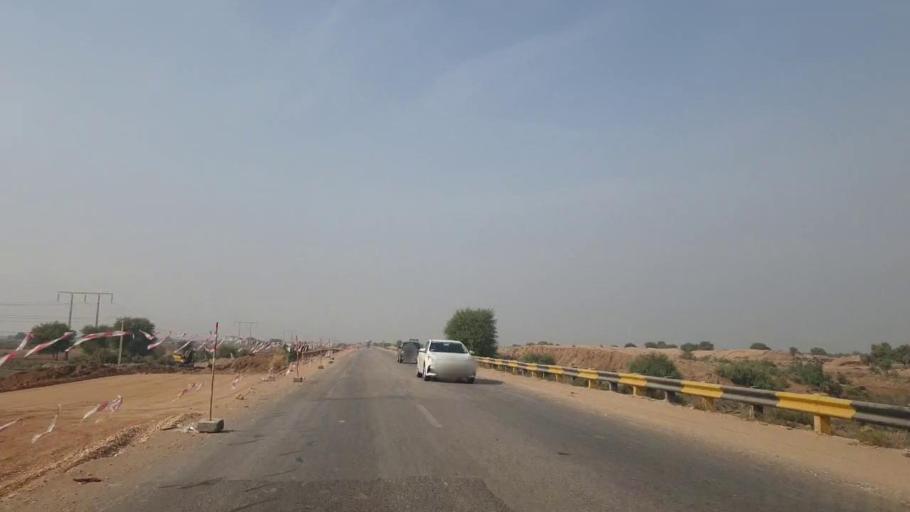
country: PK
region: Sindh
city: Sann
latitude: 26.1408
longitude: 68.0385
